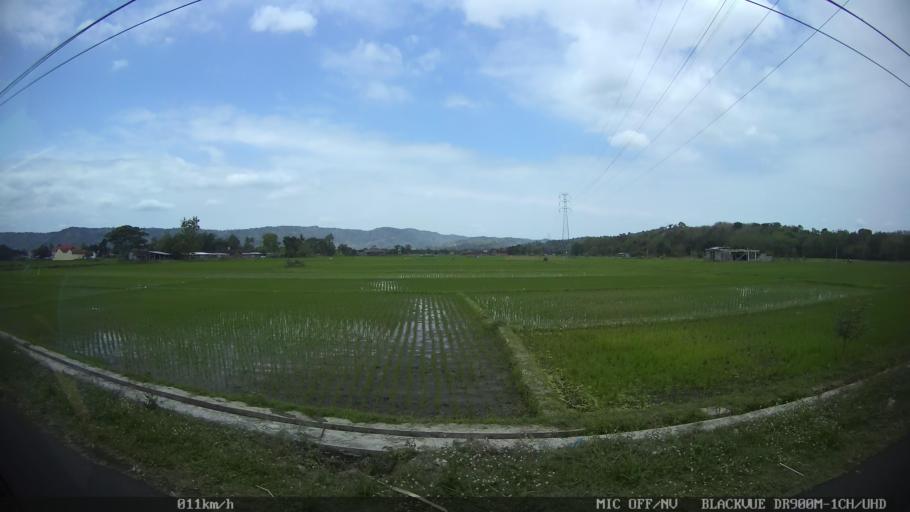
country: ID
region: Daerah Istimewa Yogyakarta
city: Depok
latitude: -7.8123
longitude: 110.4666
